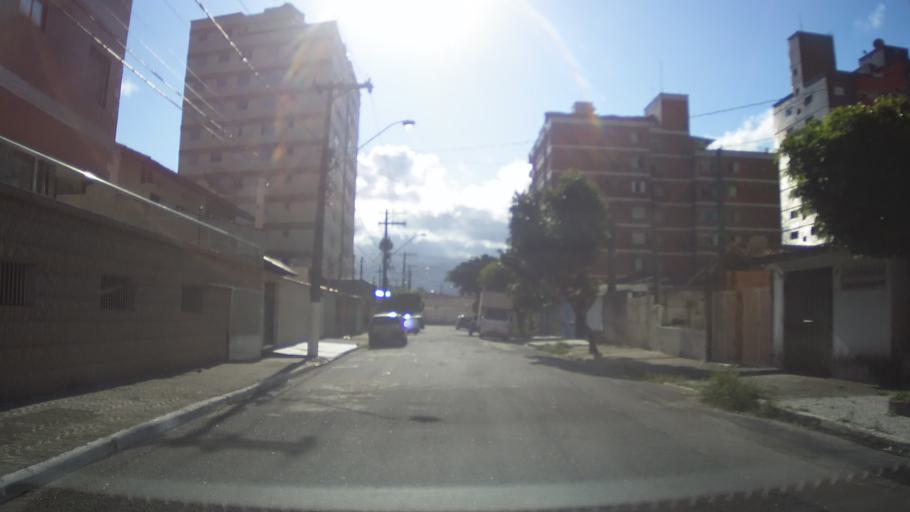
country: BR
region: Sao Paulo
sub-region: Praia Grande
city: Praia Grande
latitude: -24.0244
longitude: -46.4637
